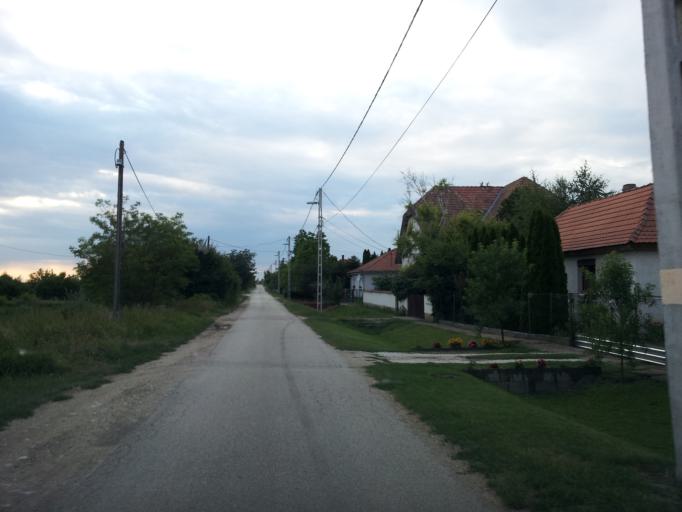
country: HU
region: Somogy
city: Balatonszabadi
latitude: 46.8854
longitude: 18.1575
